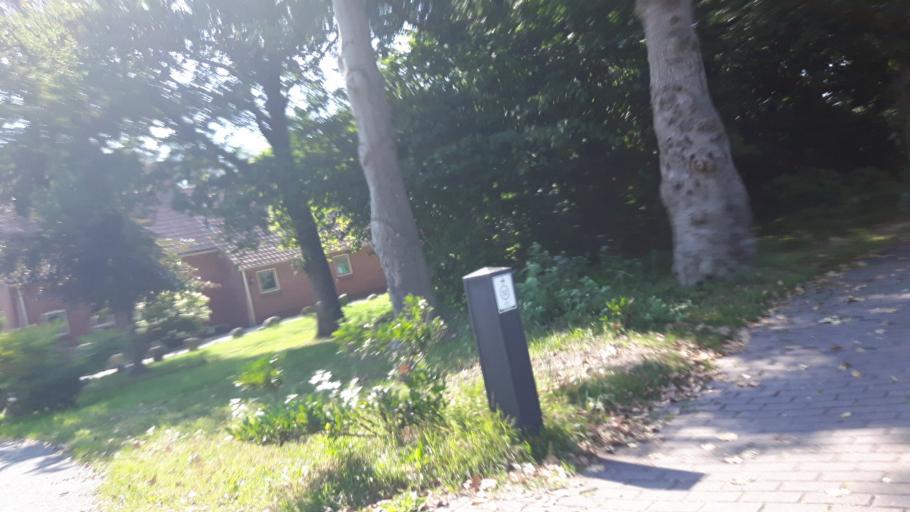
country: NL
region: Groningen
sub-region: Gemeente Hoogezand-Sappemeer
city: Hoogezand
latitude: 53.1317
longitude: 6.7225
